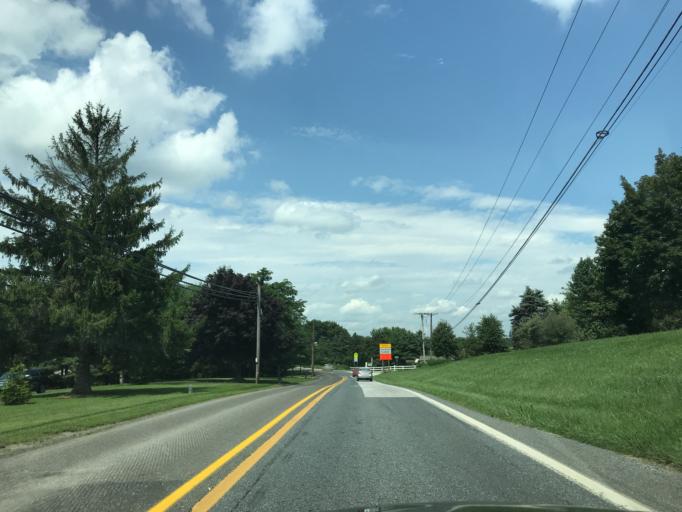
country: US
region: Pennsylvania
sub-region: York County
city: New Freedom
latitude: 39.6638
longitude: -76.7064
